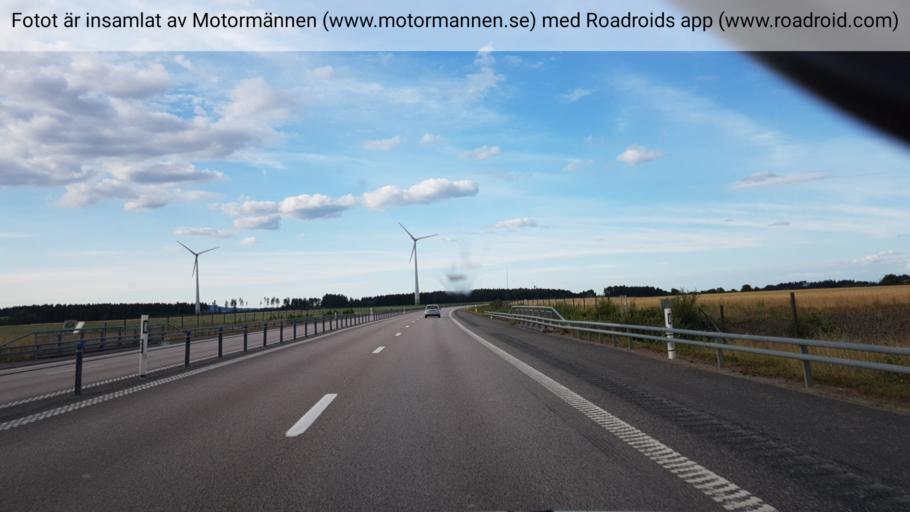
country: SE
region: Vaestra Goetaland
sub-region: Gotene Kommun
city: Goetene
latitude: 58.4743
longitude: 13.4778
